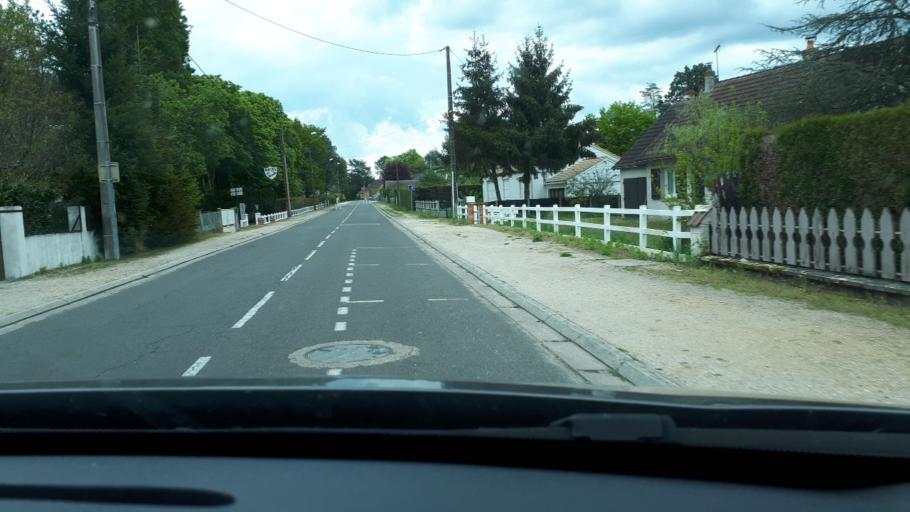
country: FR
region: Centre
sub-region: Departement du Loir-et-Cher
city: Nouan-le-Fuzelier
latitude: 47.5357
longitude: 2.0412
